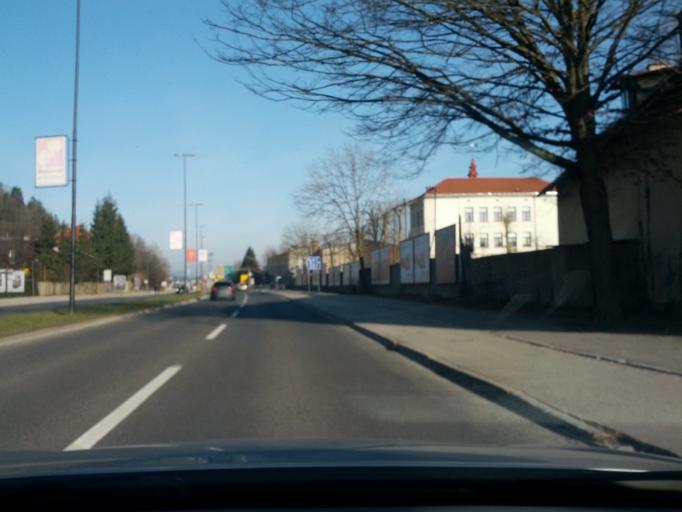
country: SI
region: Ljubljana
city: Ljubljana
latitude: 46.0951
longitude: 14.4673
